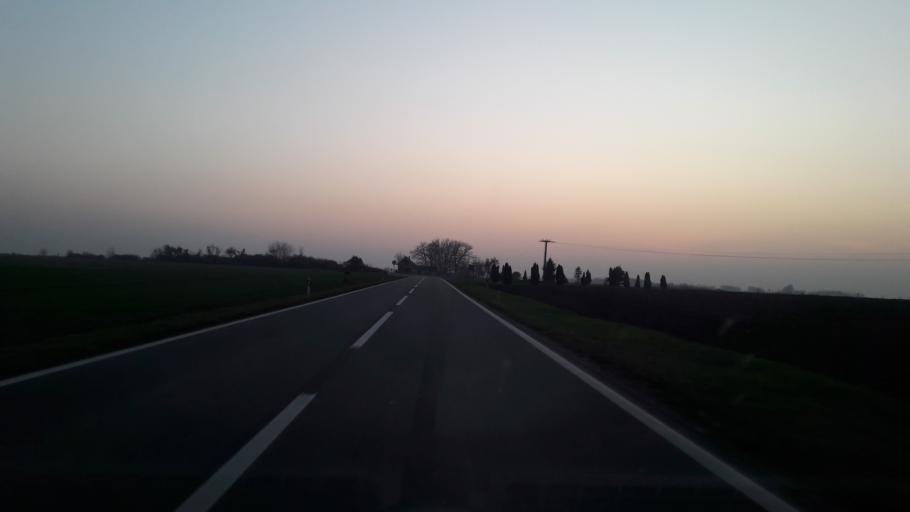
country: HR
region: Vukovarsko-Srijemska
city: Negoslavci
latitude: 45.2640
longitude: 18.9888
